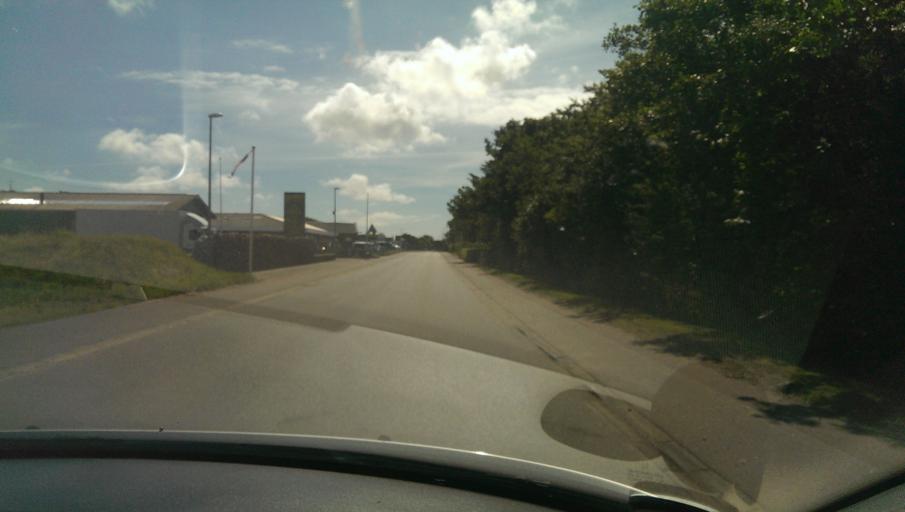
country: DK
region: Central Jutland
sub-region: Ringkobing-Skjern Kommune
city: Ringkobing
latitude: 56.1307
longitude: 8.1821
